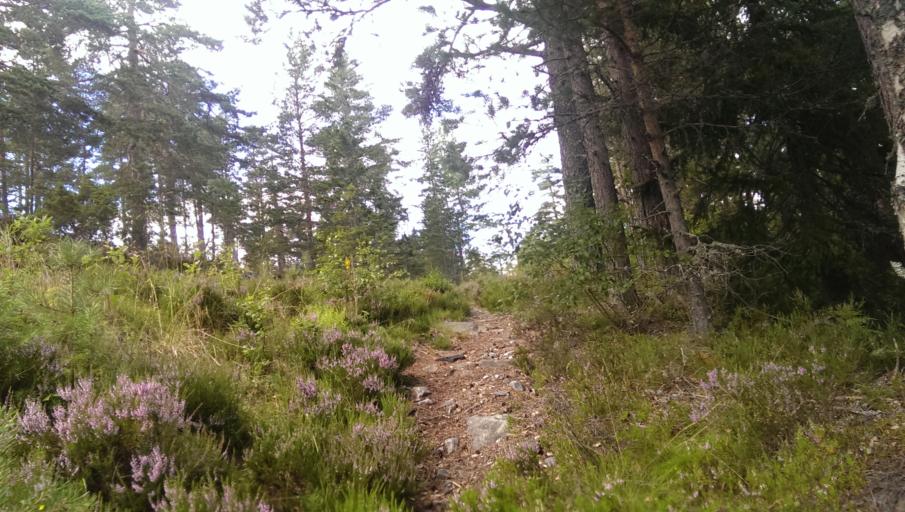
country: NO
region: Buskerud
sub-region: Kongsberg
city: Kongsberg
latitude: 59.6520
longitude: 9.6104
